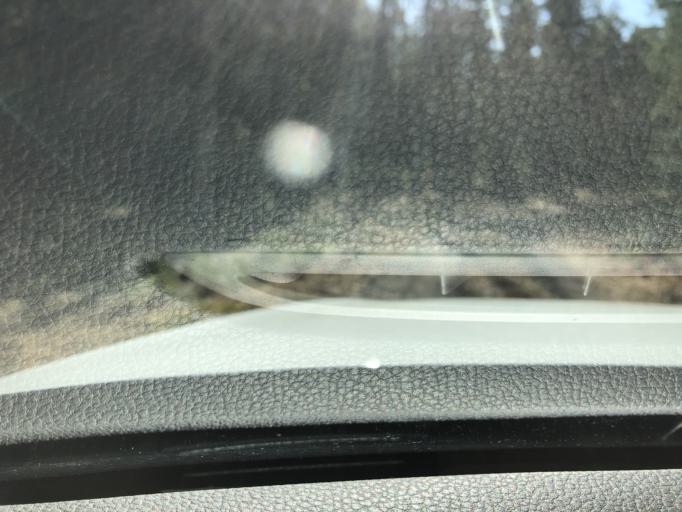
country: SE
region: Uppsala
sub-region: Heby Kommun
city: OEstervala
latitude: 60.3276
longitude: 17.1743
